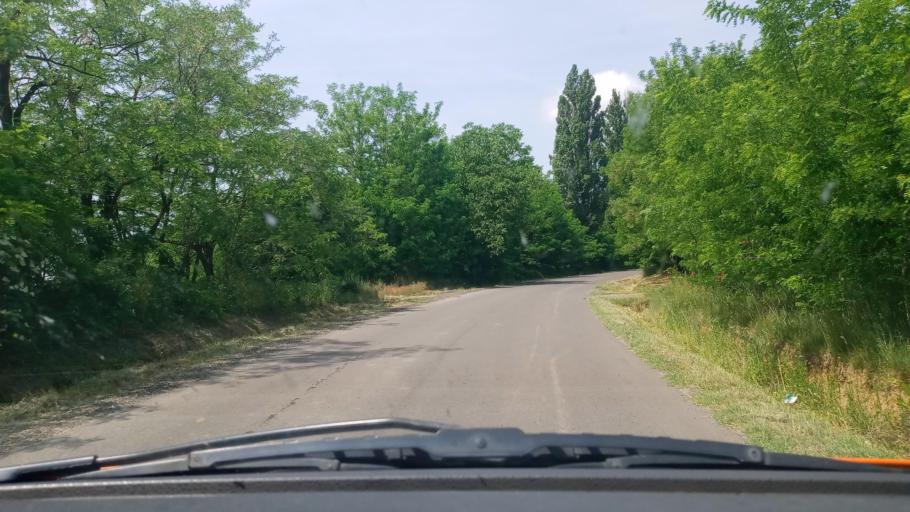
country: HU
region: Baranya
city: Szigetvar
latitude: 45.9779
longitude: 17.7162
